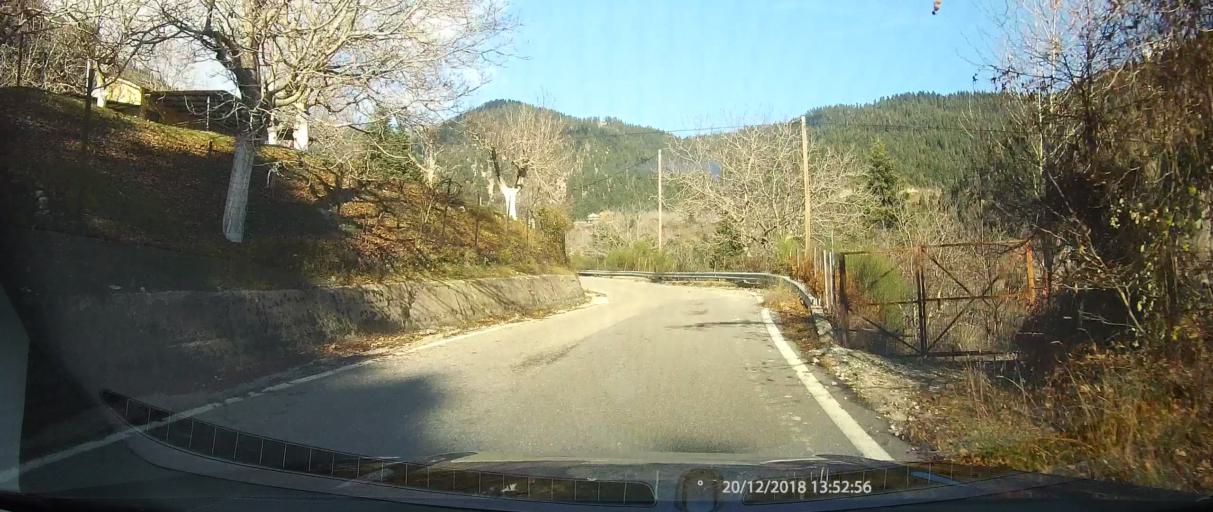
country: GR
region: West Greece
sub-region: Nomos Aitolias kai Akarnanias
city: Paravola
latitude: 38.7081
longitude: 21.6065
